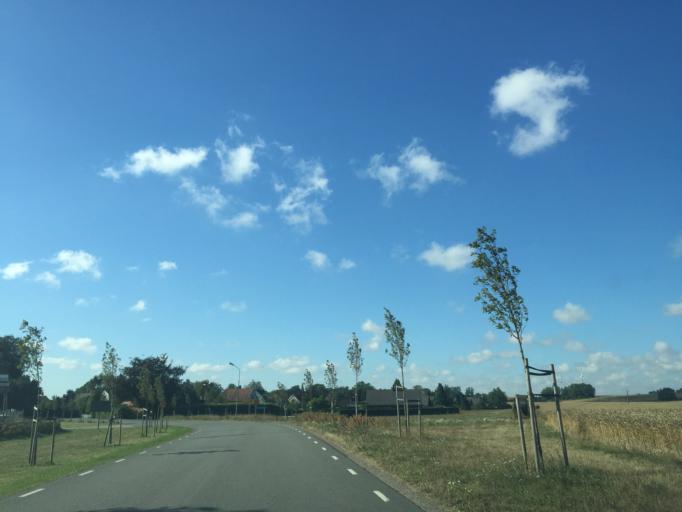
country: SE
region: Skane
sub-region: Ystads Kommun
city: Kopingebro
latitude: 55.4482
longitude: 14.0266
